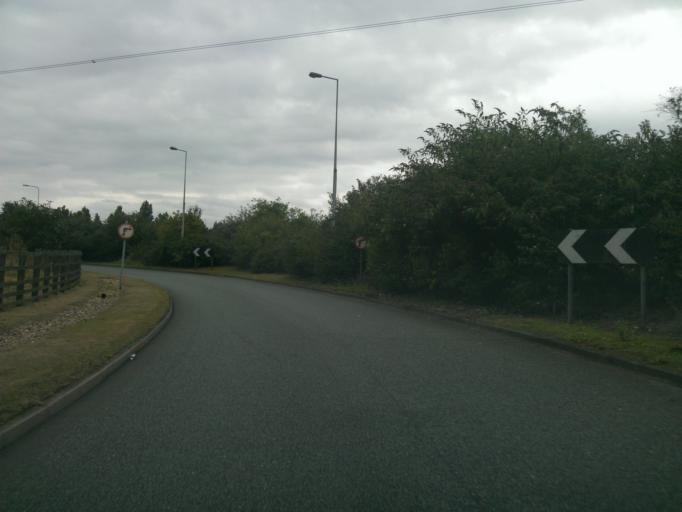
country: GB
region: England
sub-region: Kent
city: West Thurrock
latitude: 51.4895
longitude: 0.2687
